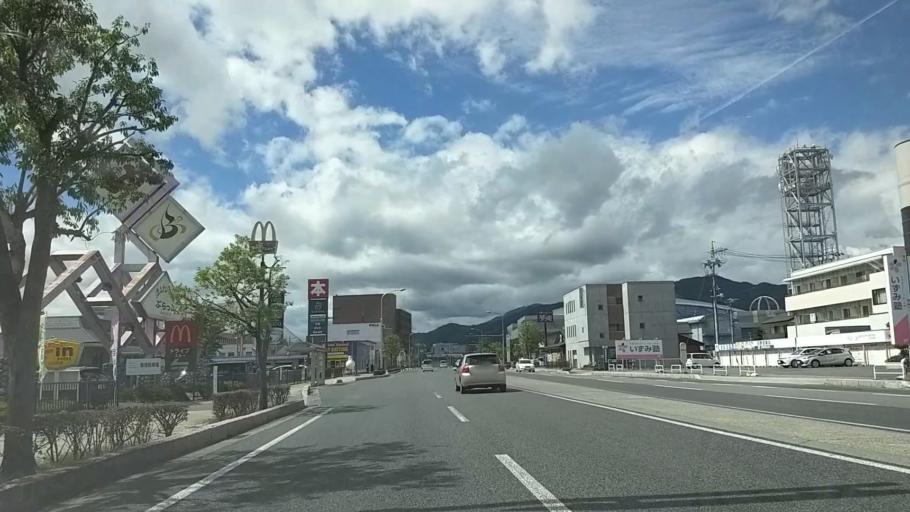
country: JP
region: Nagano
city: Nagano-shi
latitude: 36.6287
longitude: 138.1997
